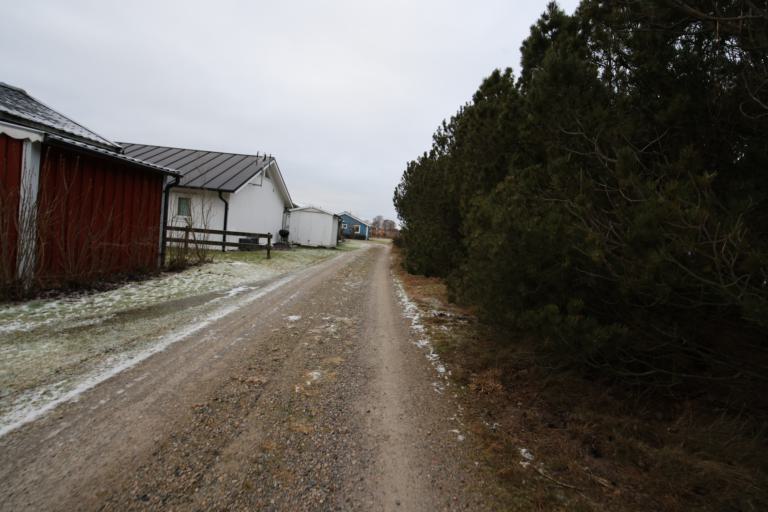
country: SE
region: Halland
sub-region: Varbergs Kommun
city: Traslovslage
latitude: 57.0705
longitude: 12.2815
